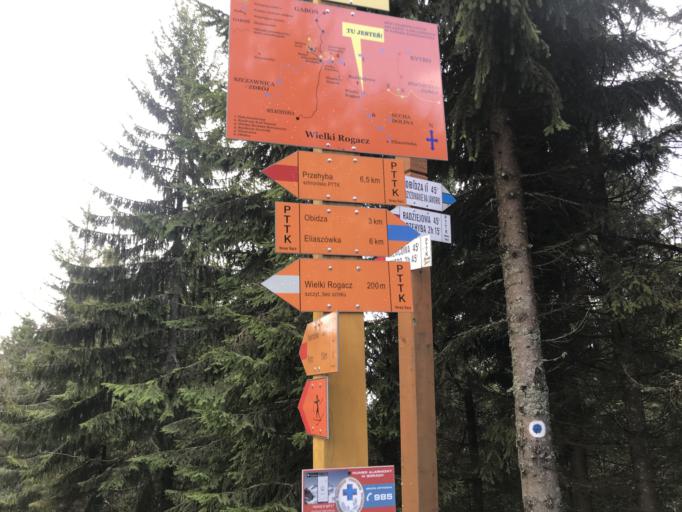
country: PL
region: Lesser Poland Voivodeship
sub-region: Powiat nowosadecki
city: Rytro
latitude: 49.4382
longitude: 20.6105
